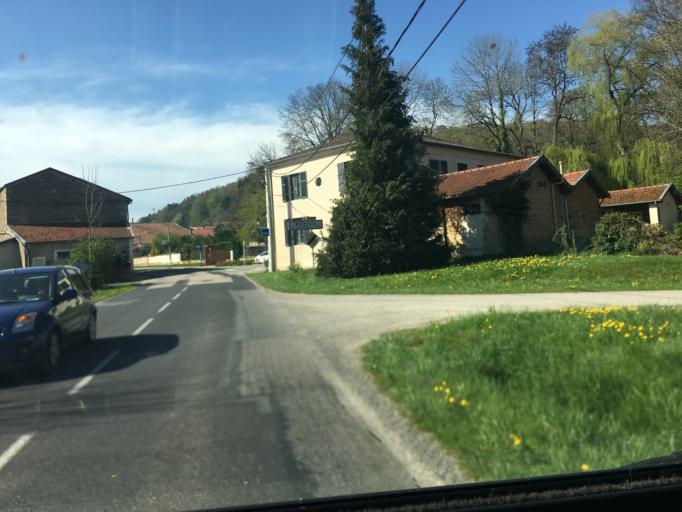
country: FR
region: Lorraine
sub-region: Departement de la Meuse
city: Vigneulles-les-Hattonchatel
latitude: 48.8977
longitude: 5.6599
